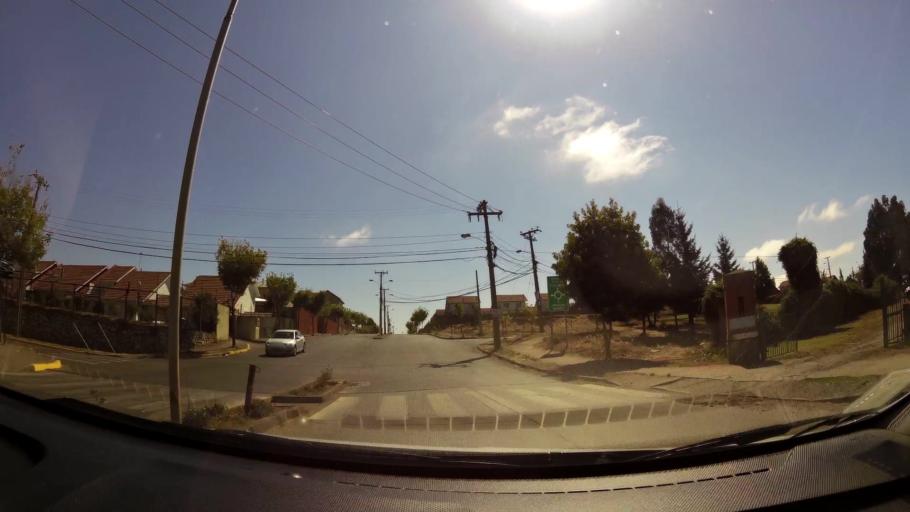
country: CL
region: Biobio
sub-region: Provincia de Concepcion
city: Concepcion
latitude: -36.7856
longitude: -73.0381
